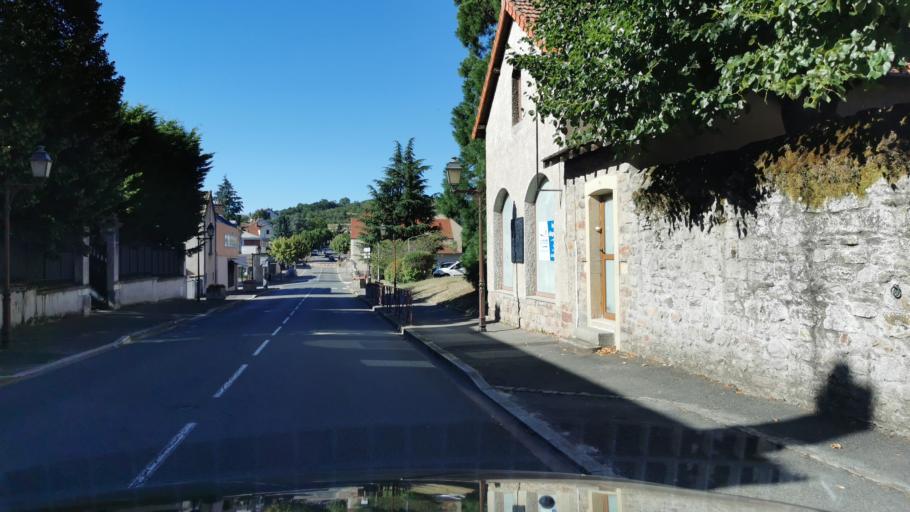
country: FR
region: Bourgogne
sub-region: Departement de Saone-et-Loire
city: Montcenis
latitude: 46.7922
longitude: 4.3889
